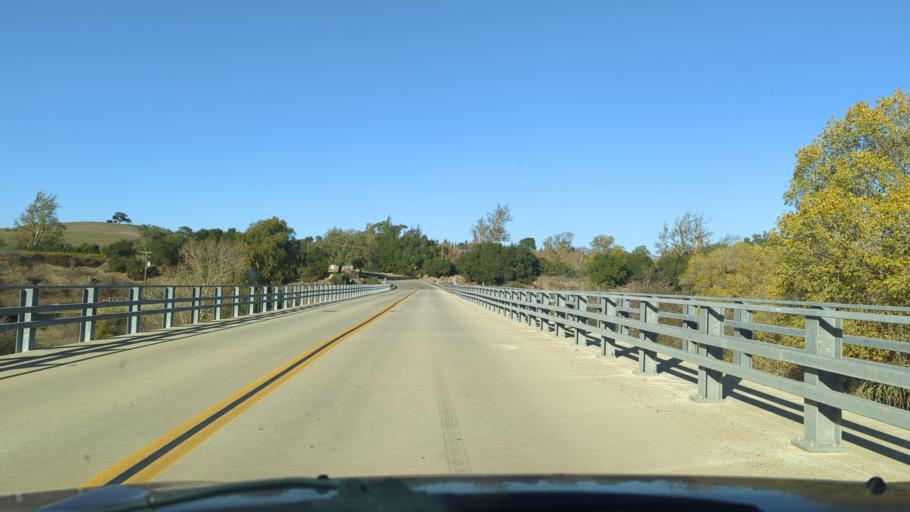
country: US
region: California
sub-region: Santa Barbara County
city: Santa Ynez
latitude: 34.5853
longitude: -120.1004
